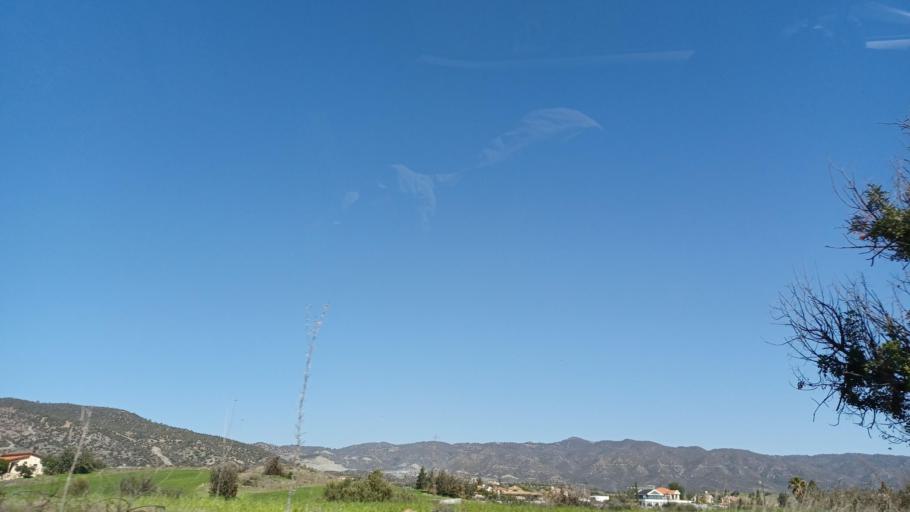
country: CY
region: Limassol
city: Parekklisha
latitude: 34.7510
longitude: 33.1494
